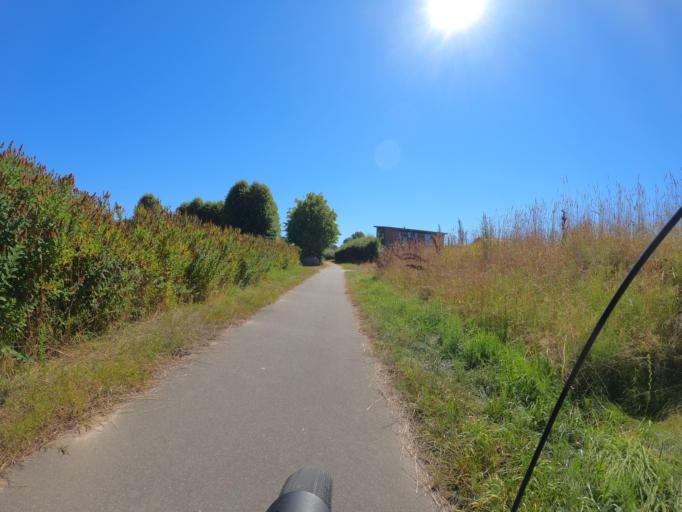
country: DE
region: Schleswig-Holstein
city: Quern
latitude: 54.7841
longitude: 9.7259
